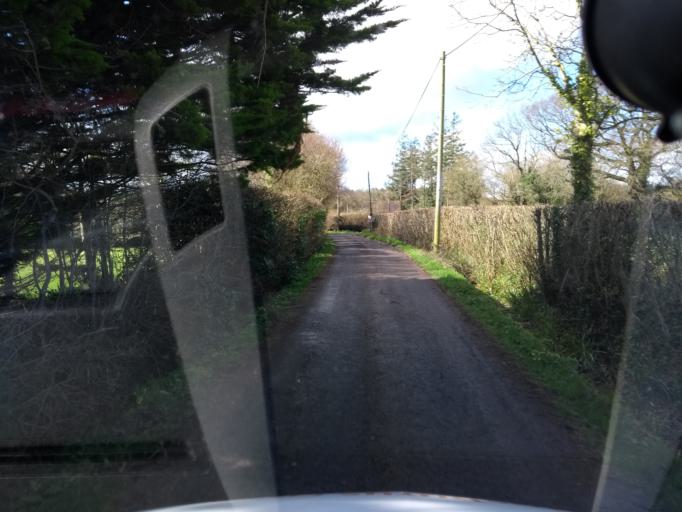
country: GB
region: England
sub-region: Somerset
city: Creech Saint Michael
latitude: 50.9718
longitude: -3.0270
